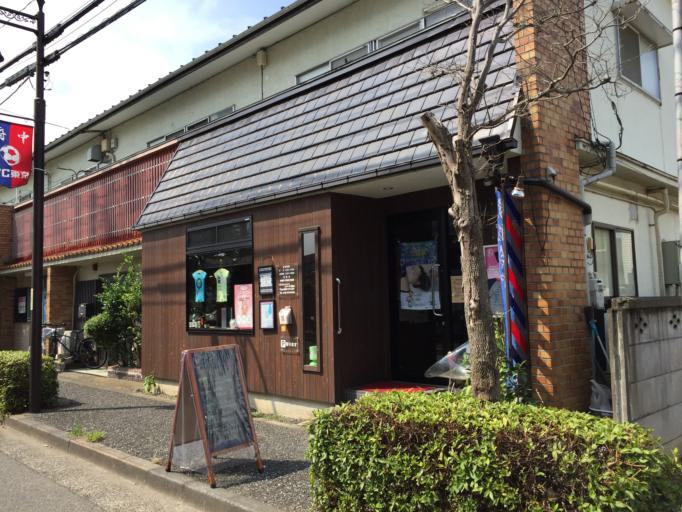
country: JP
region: Tokyo
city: Chofugaoka
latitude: 35.6651
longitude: 139.5118
